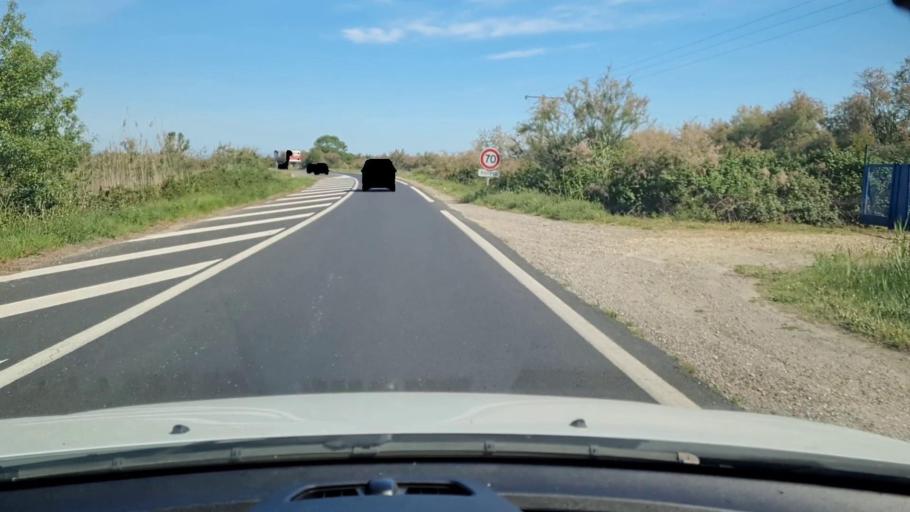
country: FR
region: Languedoc-Roussillon
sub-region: Departement de l'Herault
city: La Grande-Motte
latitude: 43.5755
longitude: 4.1041
